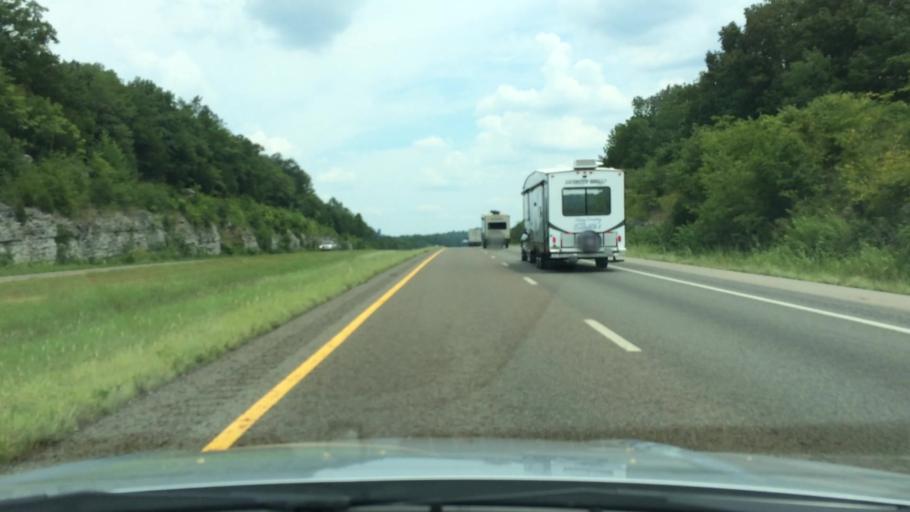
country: US
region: Tennessee
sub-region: Maury County
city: Columbia
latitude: 35.6087
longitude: -86.9007
